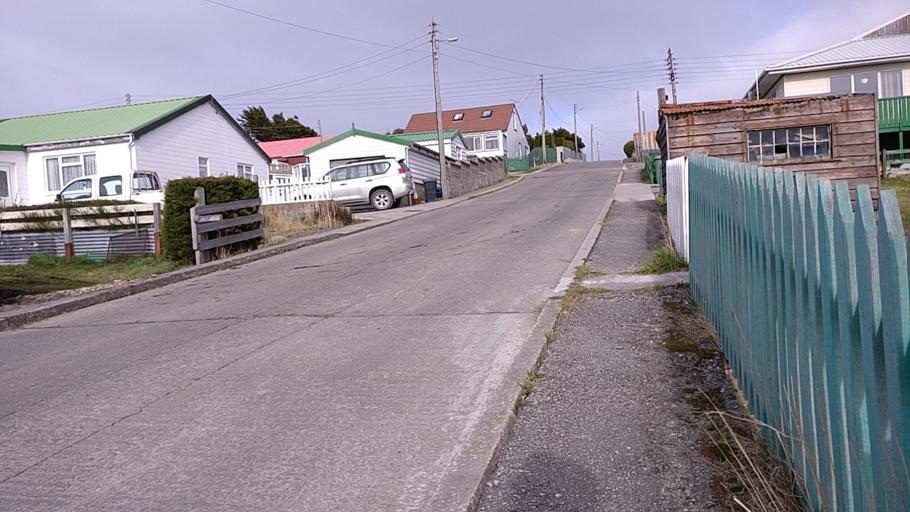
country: FK
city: Stanley
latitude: -51.6943
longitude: -57.8634
